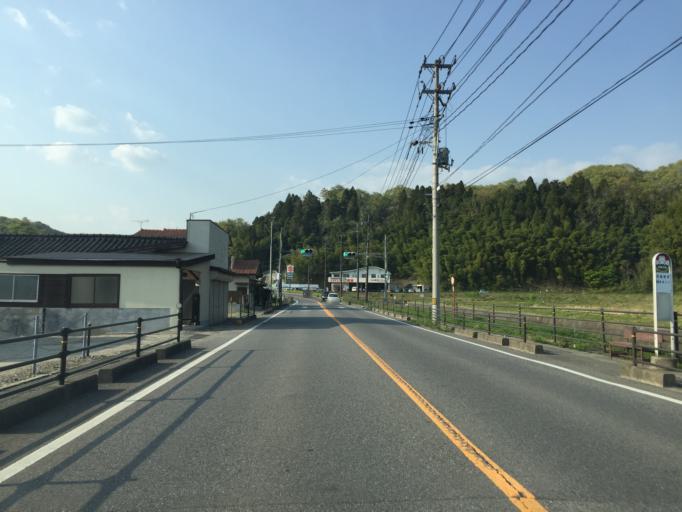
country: JP
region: Fukushima
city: Iwaki
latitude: 37.0162
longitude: 140.8467
